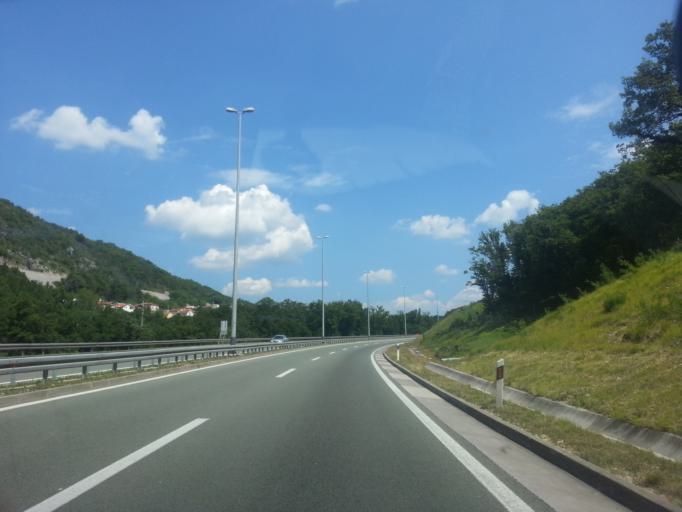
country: HR
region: Primorsko-Goranska
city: Skrljevo
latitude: 45.3163
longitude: 14.5079
